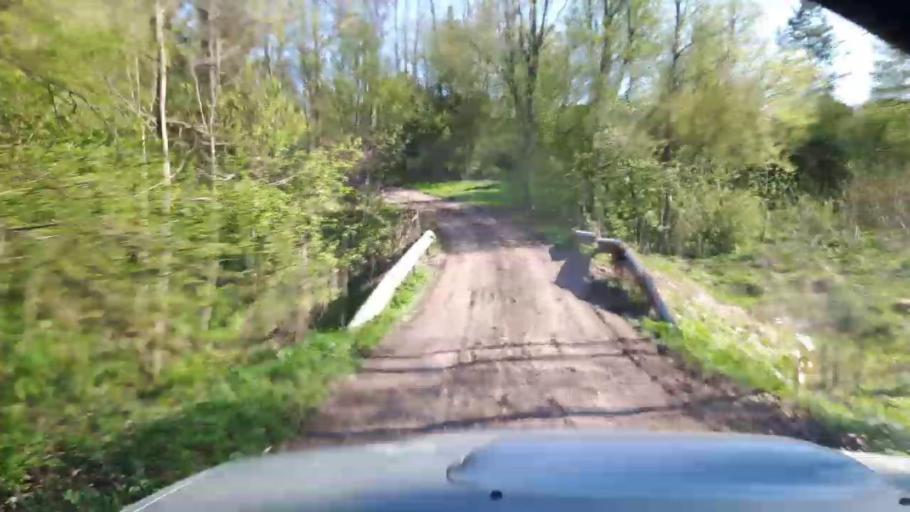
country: EE
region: Paernumaa
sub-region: Tootsi vald
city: Tootsi
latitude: 58.4841
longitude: 24.8254
